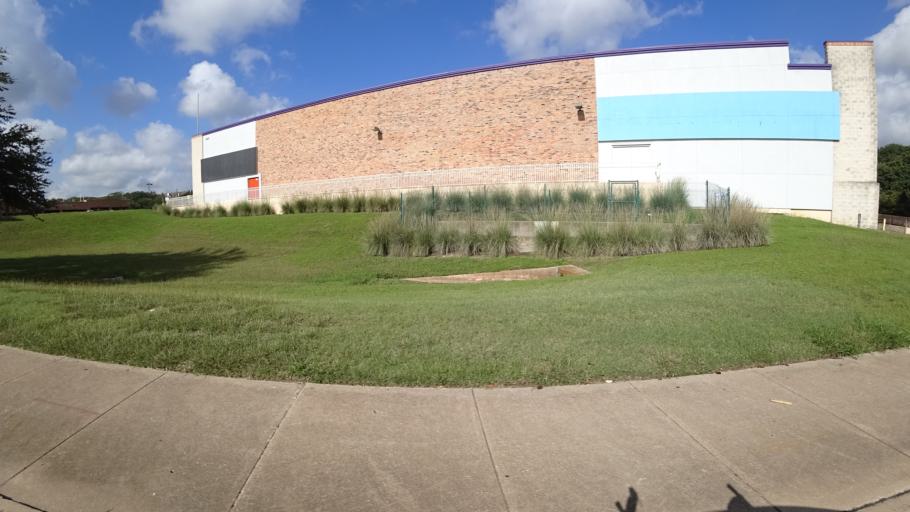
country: US
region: Texas
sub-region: Travis County
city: Shady Hollow
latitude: 30.2093
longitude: -97.8143
